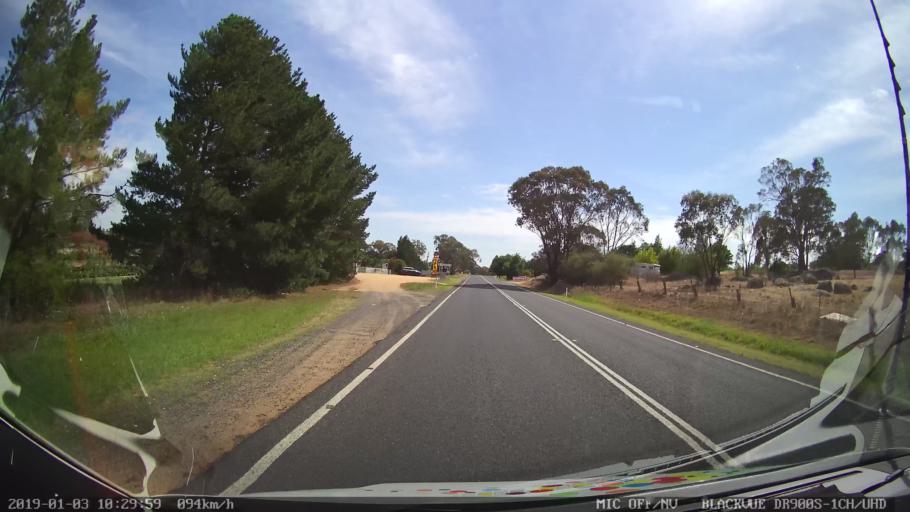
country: AU
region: New South Wales
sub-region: Young
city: Young
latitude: -34.3671
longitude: 148.2633
